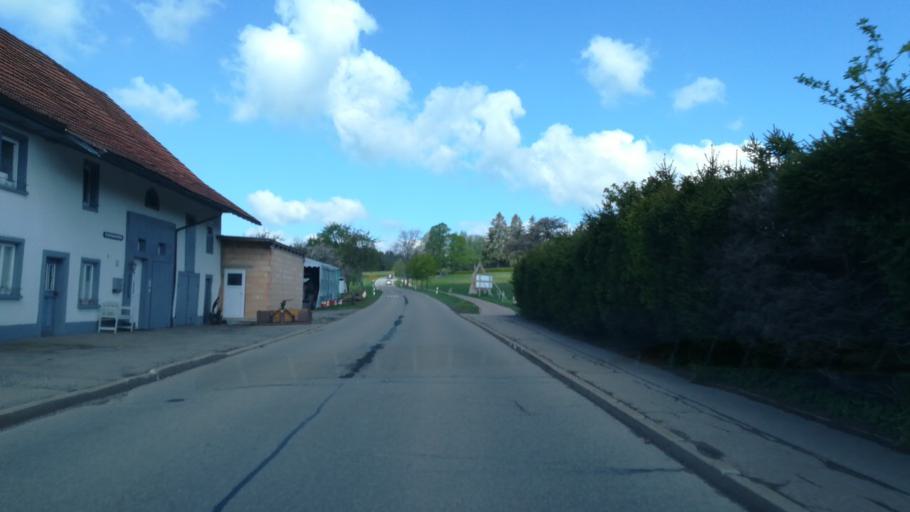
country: DE
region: Baden-Wuerttemberg
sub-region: Freiburg Region
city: Uhlingen-Birkendorf
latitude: 47.7520
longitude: 8.3076
